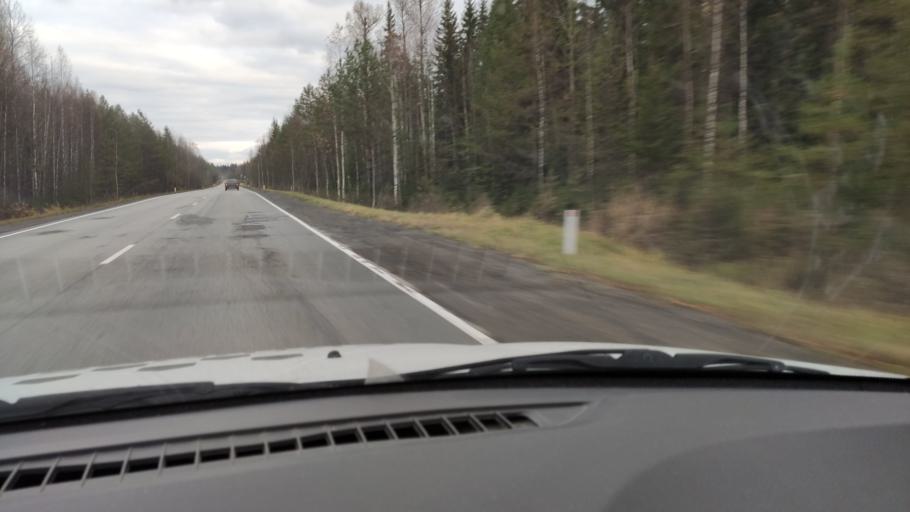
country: RU
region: Kirov
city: Chernaya Kholunitsa
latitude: 58.8676
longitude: 51.5650
